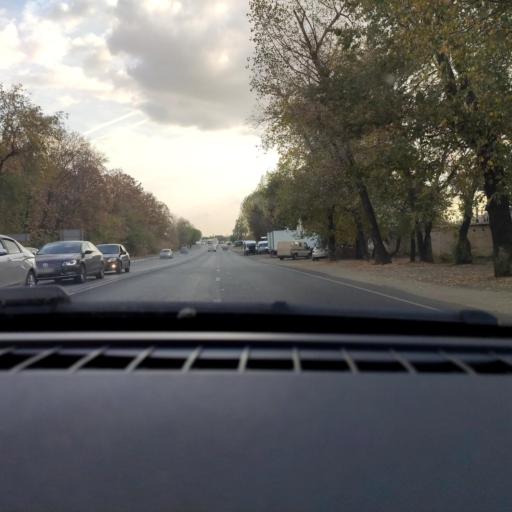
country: RU
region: Voronezj
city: Voronezh
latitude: 51.6681
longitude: 39.2712
